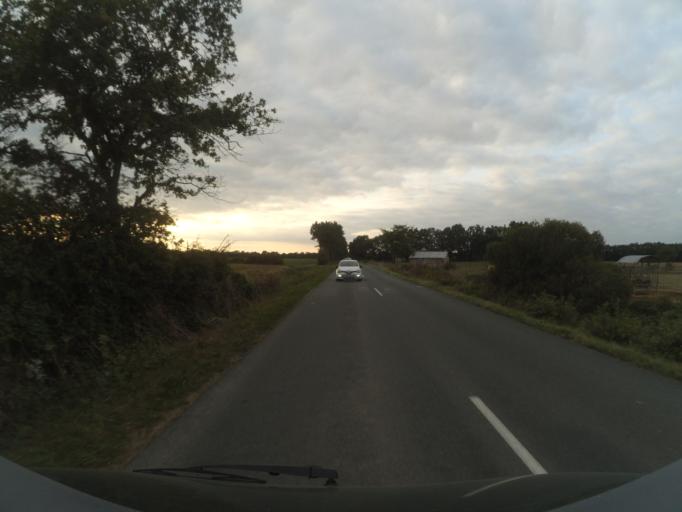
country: FR
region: Pays de la Loire
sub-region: Departement de la Loire-Atlantique
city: Montbert
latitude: 47.0114
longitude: -1.4792
